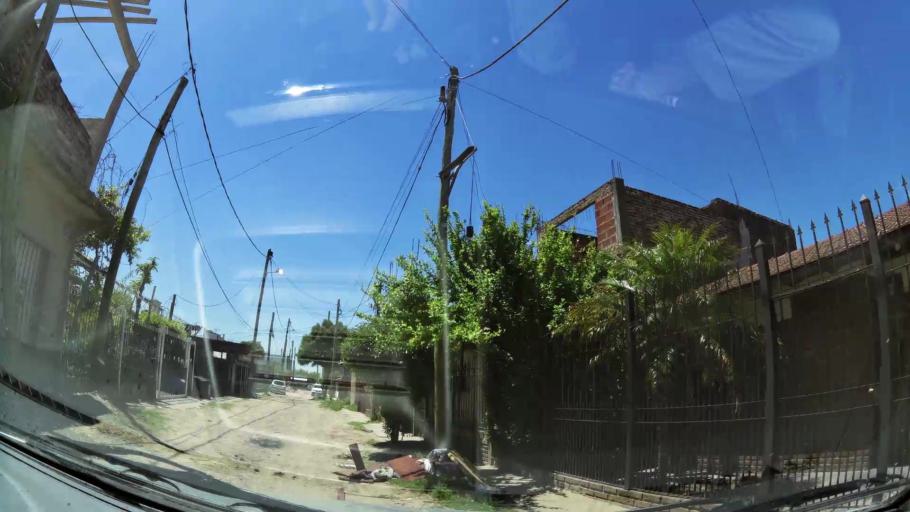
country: AR
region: Buenos Aires
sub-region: Partido de Quilmes
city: Quilmes
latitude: -34.7193
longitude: -58.3246
